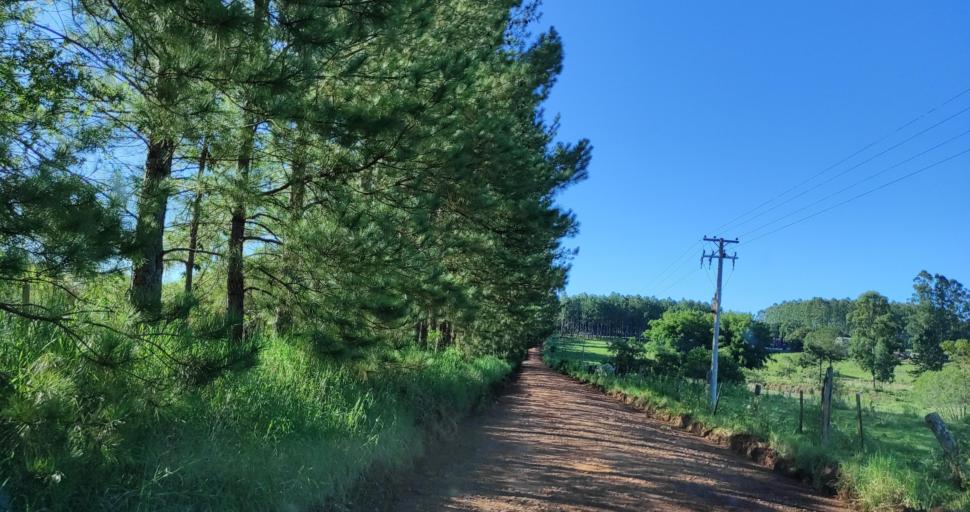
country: AR
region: Misiones
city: Puerto Rico
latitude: -26.8363
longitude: -55.0020
